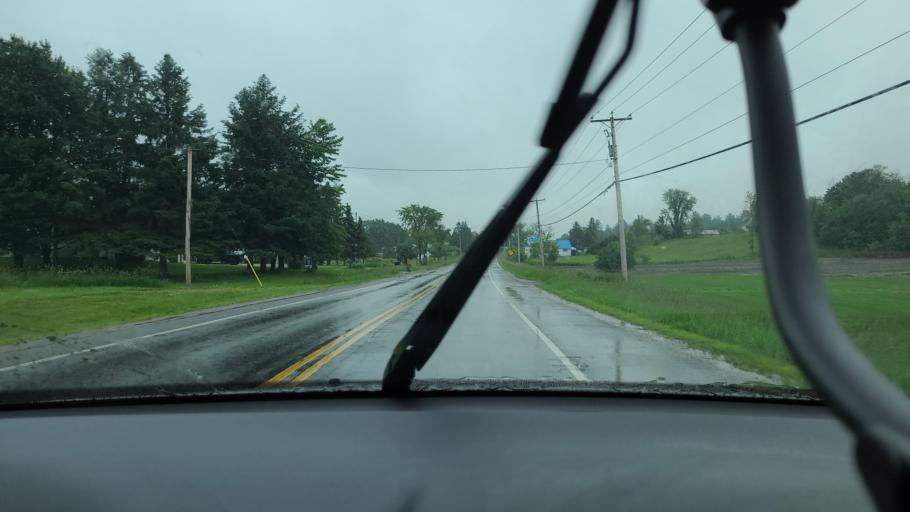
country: CA
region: Quebec
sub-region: Outaouais
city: Saint-Andre-Avellin
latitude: 45.7072
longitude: -75.0529
